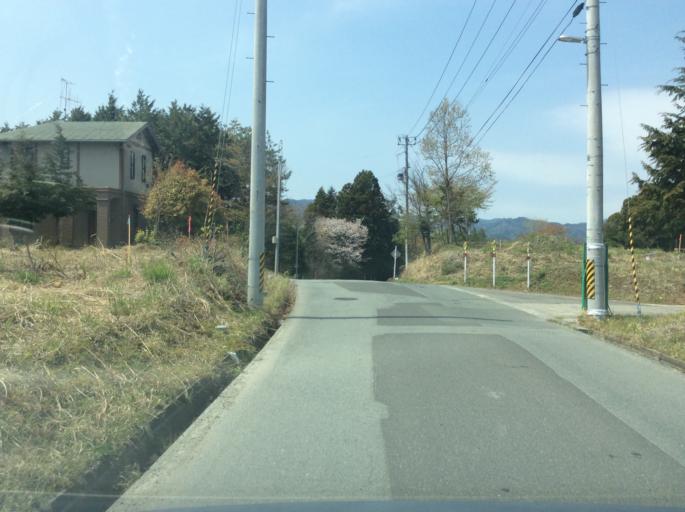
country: JP
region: Fukushima
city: Namie
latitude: 37.2711
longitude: 141.0083
